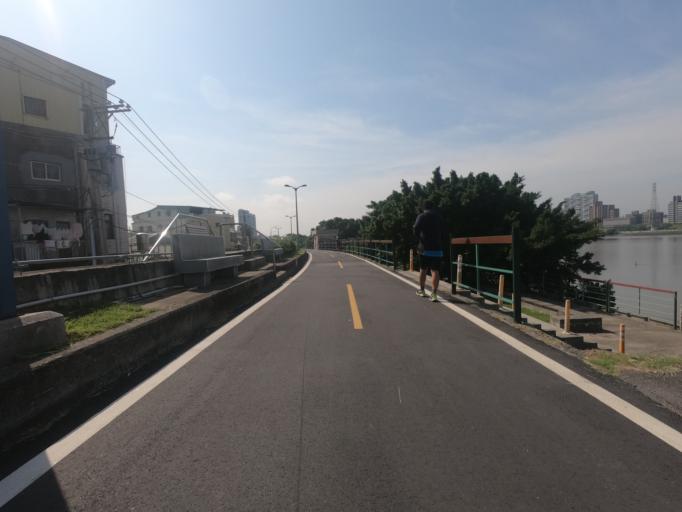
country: TW
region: Taipei
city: Taipei
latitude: 25.0958
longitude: 121.4941
